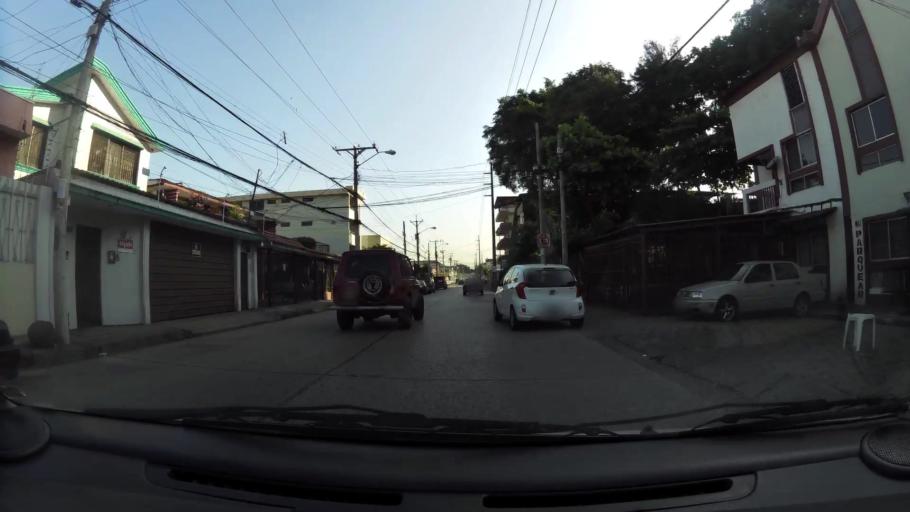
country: EC
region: Guayas
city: Guayaquil
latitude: -2.1599
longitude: -79.9038
